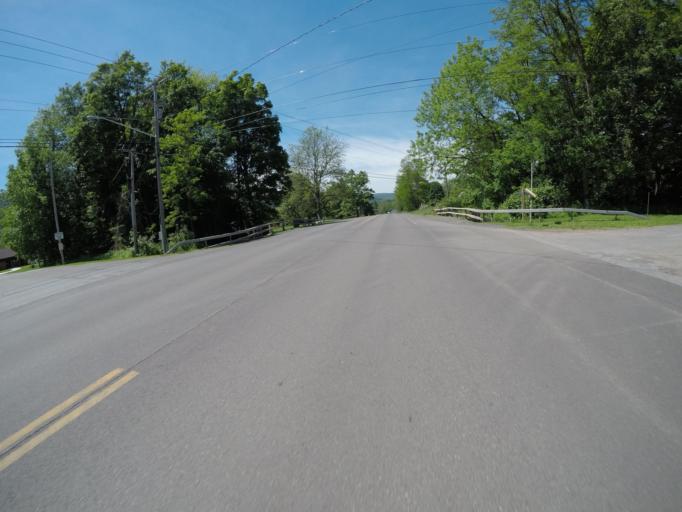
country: US
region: New York
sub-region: Delaware County
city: Walton
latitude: 42.1818
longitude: -75.0130
